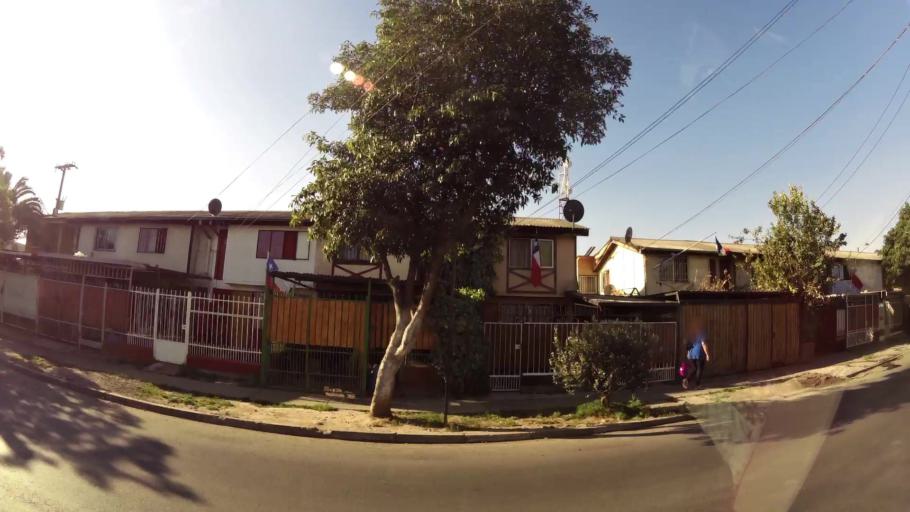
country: CL
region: Santiago Metropolitan
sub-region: Provincia de Santiago
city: La Pintana
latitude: -33.5493
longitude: -70.6269
